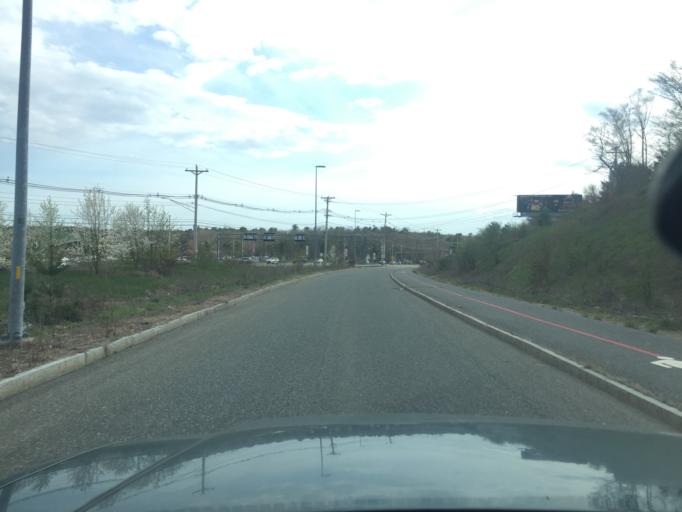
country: US
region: Massachusetts
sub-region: Norfolk County
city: Foxborough
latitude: 42.0887
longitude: -71.2734
